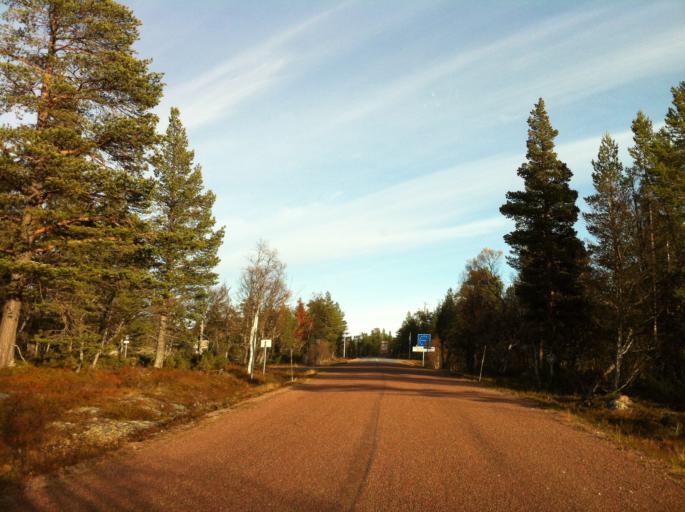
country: NO
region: Hedmark
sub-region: Engerdal
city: Engerdal
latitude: 62.0763
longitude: 12.1758
